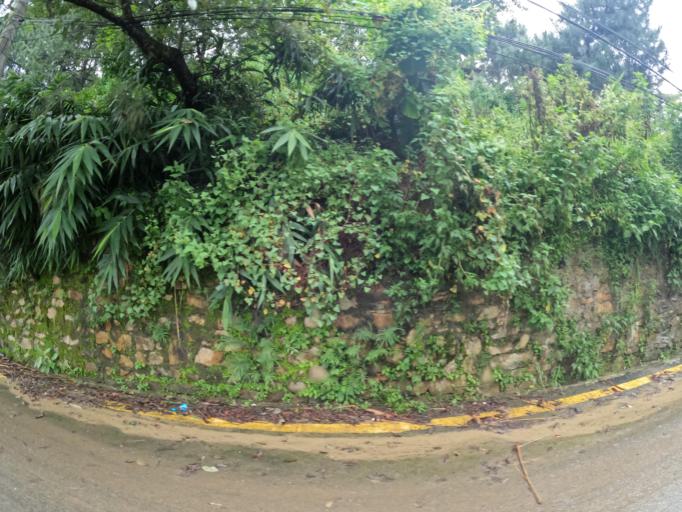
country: NP
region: Central Region
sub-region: Bagmati Zone
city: Kathmandu
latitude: 27.7630
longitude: 85.3286
